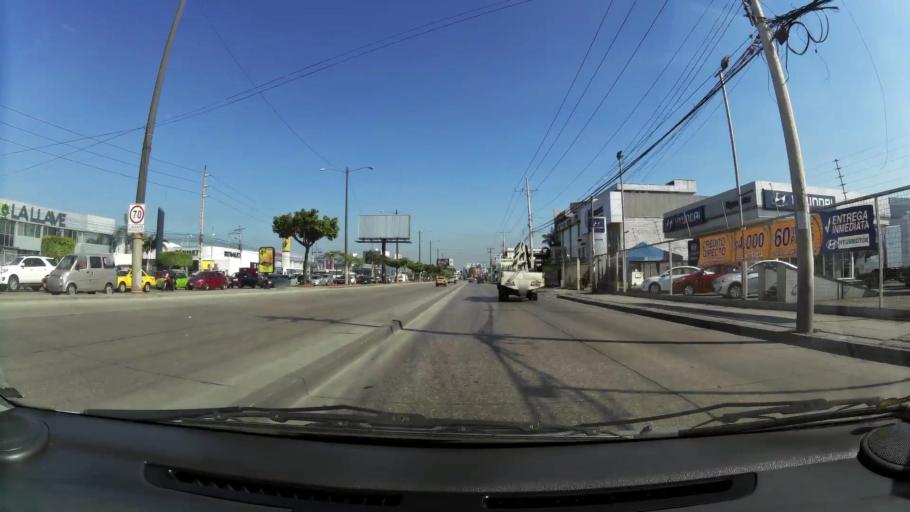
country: EC
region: Guayas
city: Eloy Alfaro
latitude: -2.1492
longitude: -79.9014
